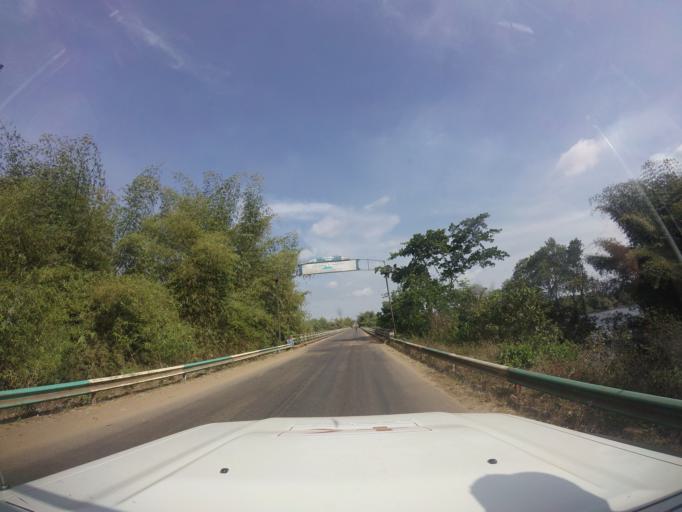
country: LR
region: Bomi
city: Tubmanburg
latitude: 6.7210
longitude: -10.9797
